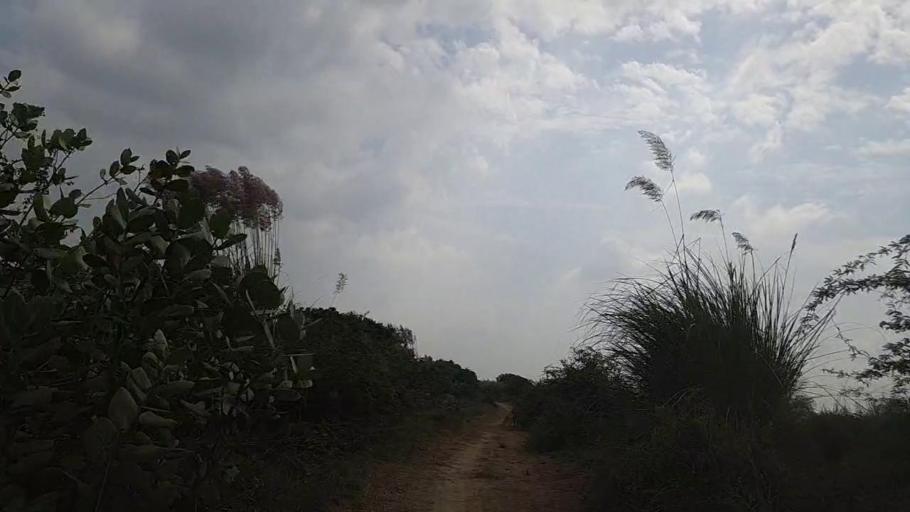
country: PK
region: Sindh
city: Mirpur Batoro
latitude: 24.6126
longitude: 68.1356
